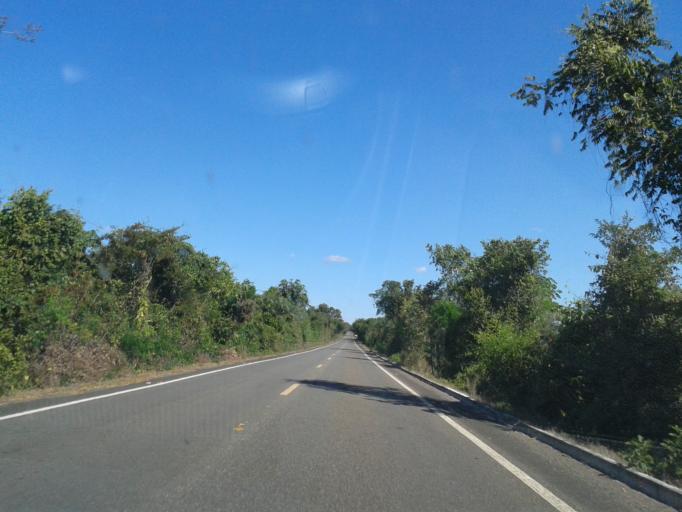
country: BR
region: Goias
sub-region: Sao Miguel Do Araguaia
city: Sao Miguel do Araguaia
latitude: -13.7925
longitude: -50.3411
